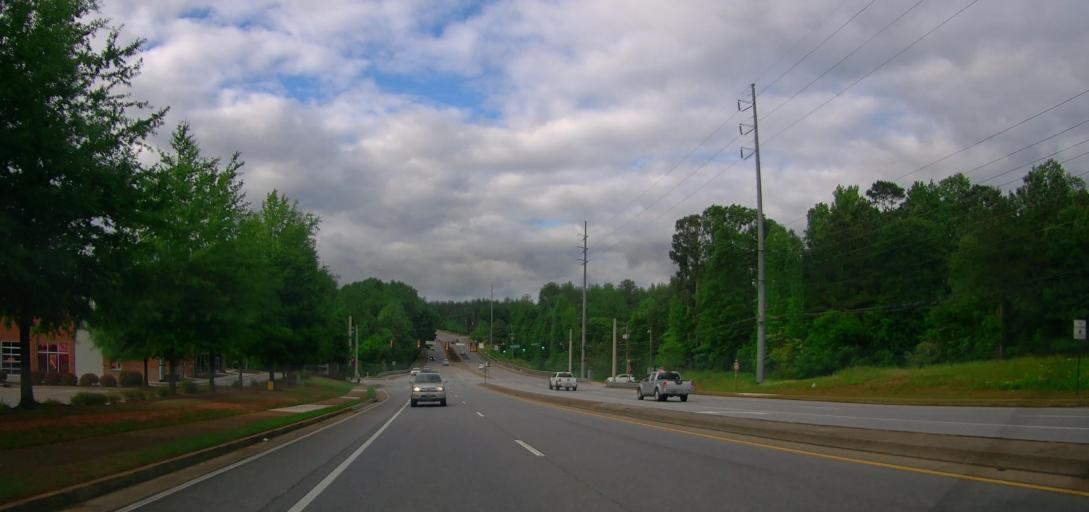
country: US
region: Georgia
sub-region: Oconee County
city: Watkinsville
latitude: 33.9216
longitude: -83.4410
